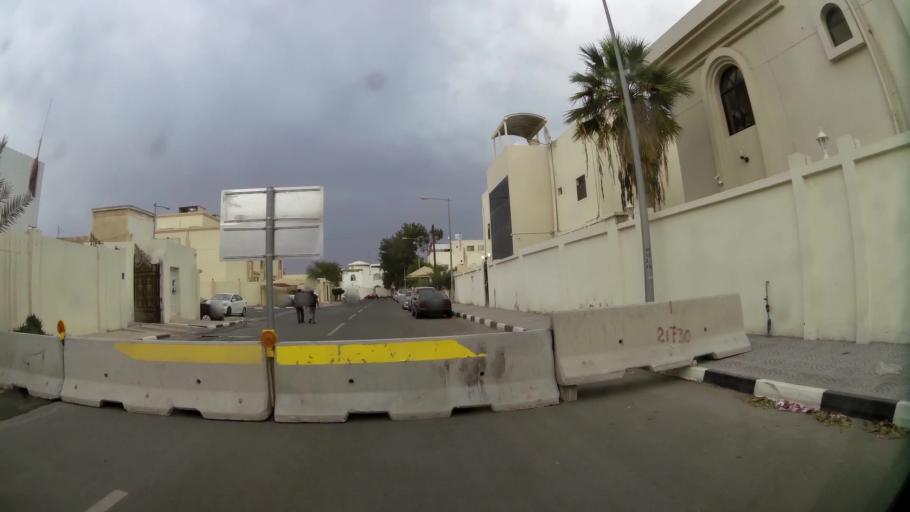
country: QA
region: Baladiyat ad Dawhah
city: Doha
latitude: 25.2686
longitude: 51.4980
